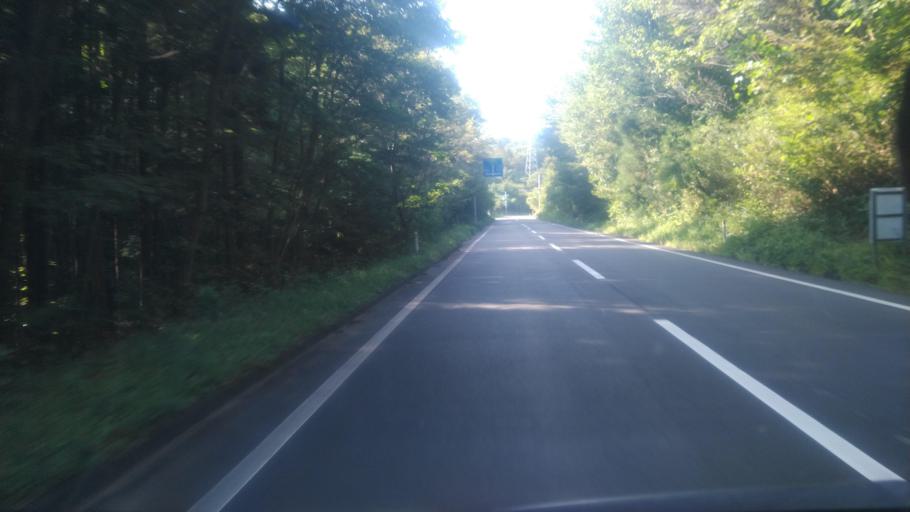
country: JP
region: Miyagi
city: Okawara
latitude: 38.0909
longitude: 140.7123
